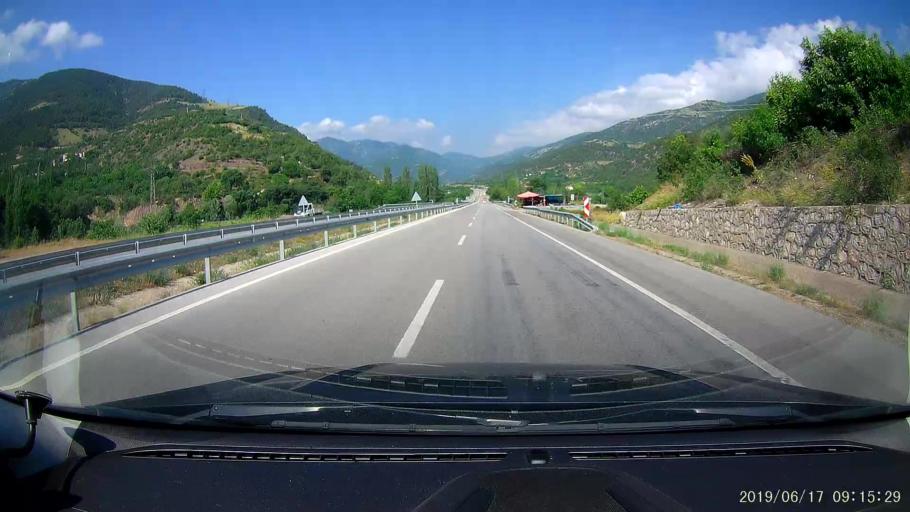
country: TR
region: Amasya
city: Akdag
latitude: 40.7467
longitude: 36.0353
